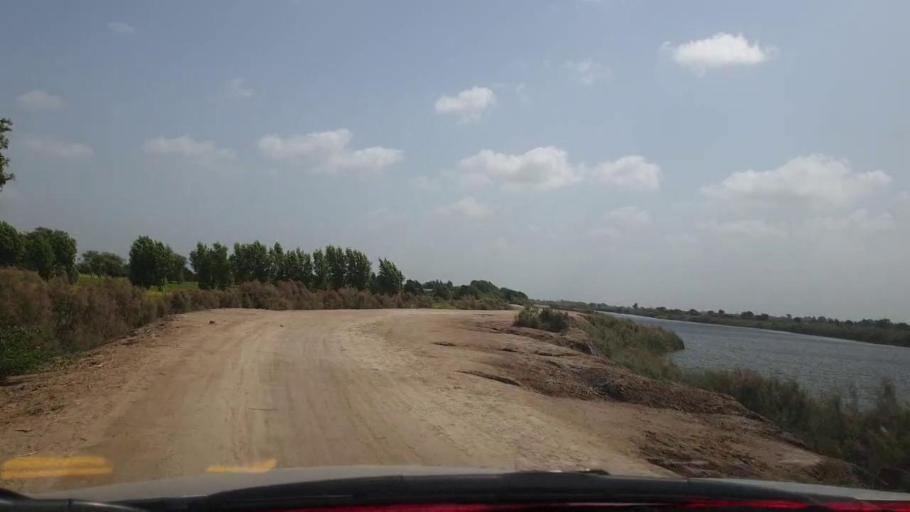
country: PK
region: Sindh
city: Talhar
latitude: 24.8750
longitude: 68.9132
